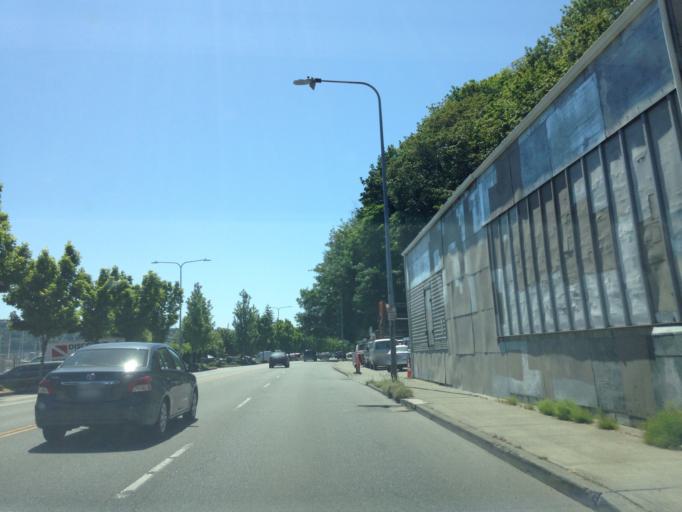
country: US
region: Washington
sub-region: King County
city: Seattle
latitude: 47.6429
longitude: -122.3441
